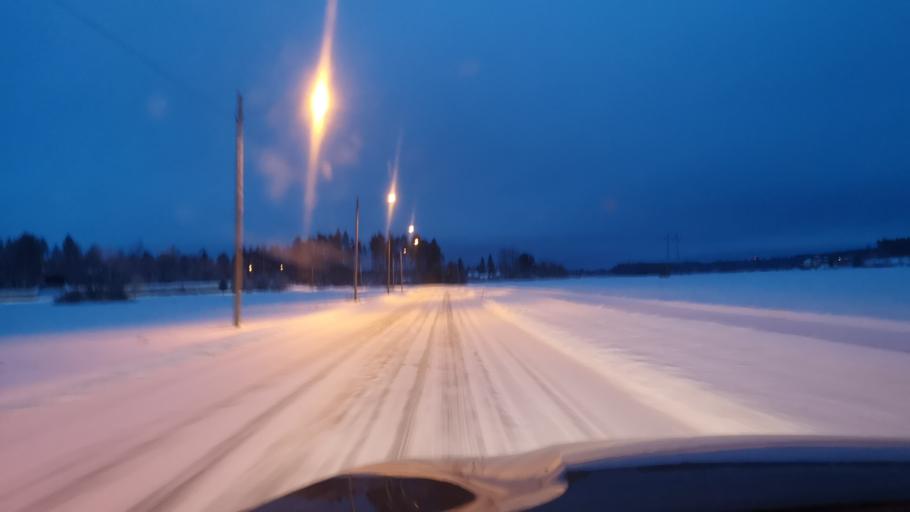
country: FI
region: Varsinais-Suomi
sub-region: Loimaa
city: Loimaa
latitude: 60.8617
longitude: 23.0773
